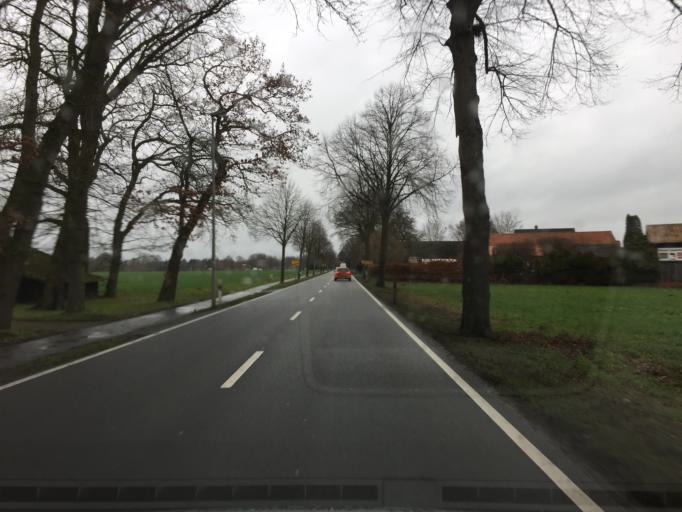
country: DE
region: Lower Saxony
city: Kirchseelte
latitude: 52.9892
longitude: 8.7180
